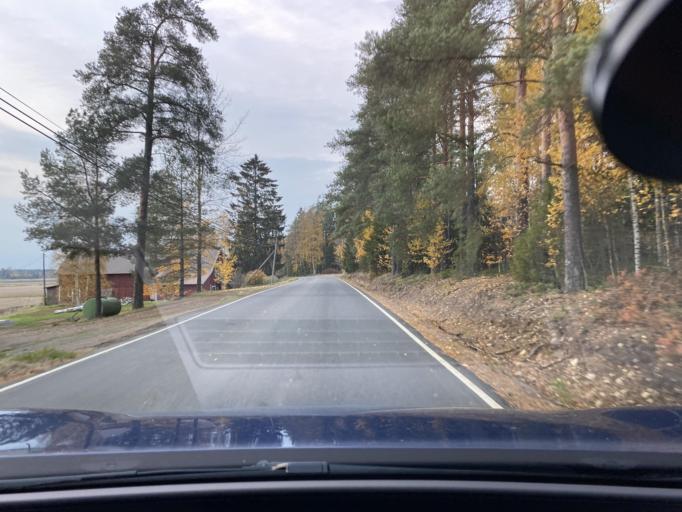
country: FI
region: Varsinais-Suomi
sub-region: Loimaa
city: Alastaro
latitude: 61.0942
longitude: 22.9038
